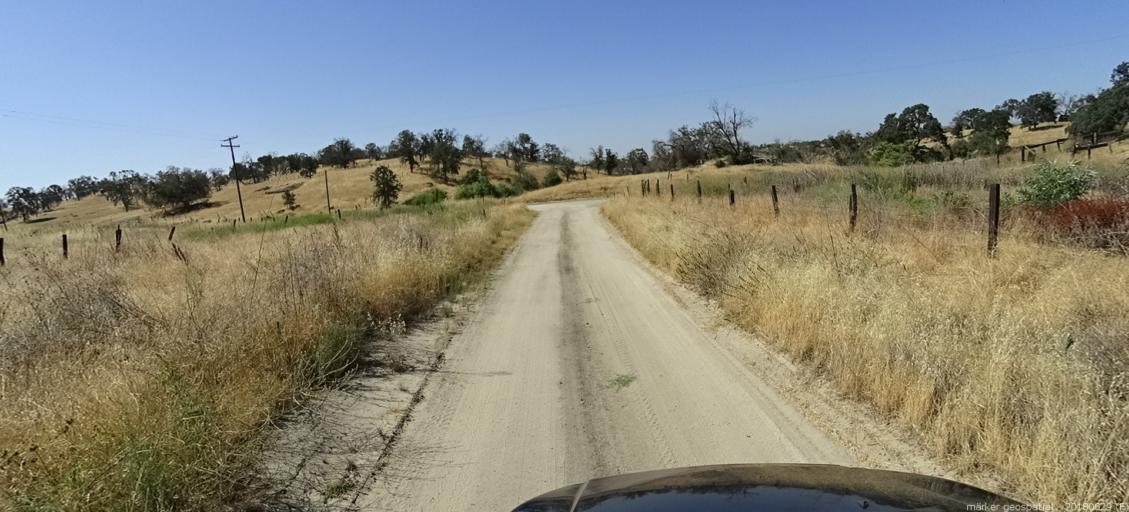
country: US
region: California
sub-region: Madera County
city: Bonadelle Ranchos-Madera Ranchos
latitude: 37.0800
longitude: -119.8324
